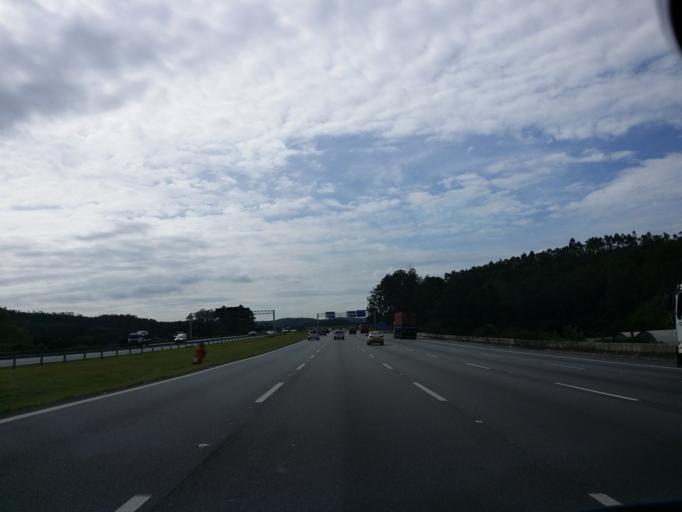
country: BR
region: Sao Paulo
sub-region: Cajamar
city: Cajamar
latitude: -23.3303
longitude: -46.8231
